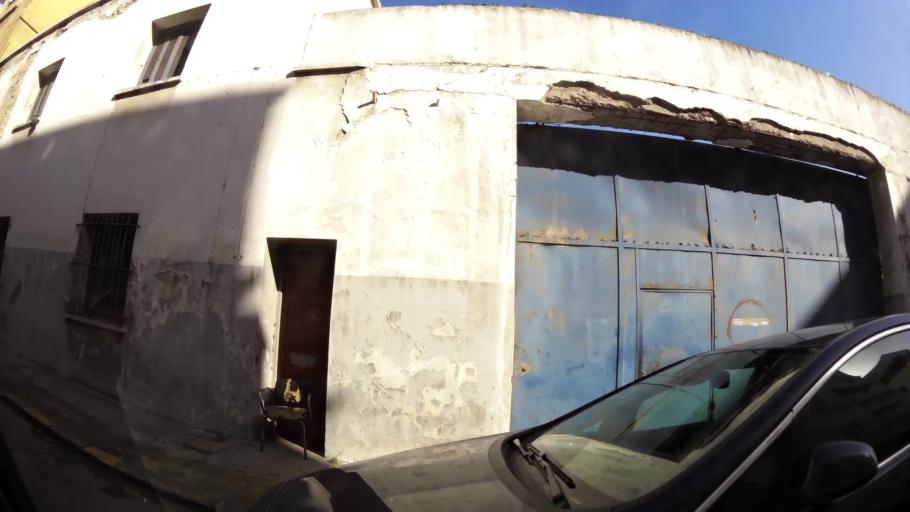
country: MA
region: Grand Casablanca
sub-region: Casablanca
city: Casablanca
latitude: 33.6007
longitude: -7.5807
